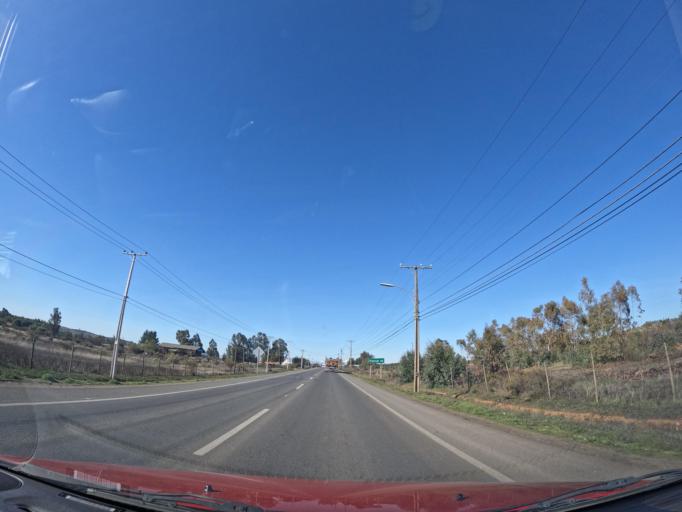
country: CL
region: Maule
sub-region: Provincia de Cauquenes
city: Cauquenes
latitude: -35.9583
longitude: -72.2719
